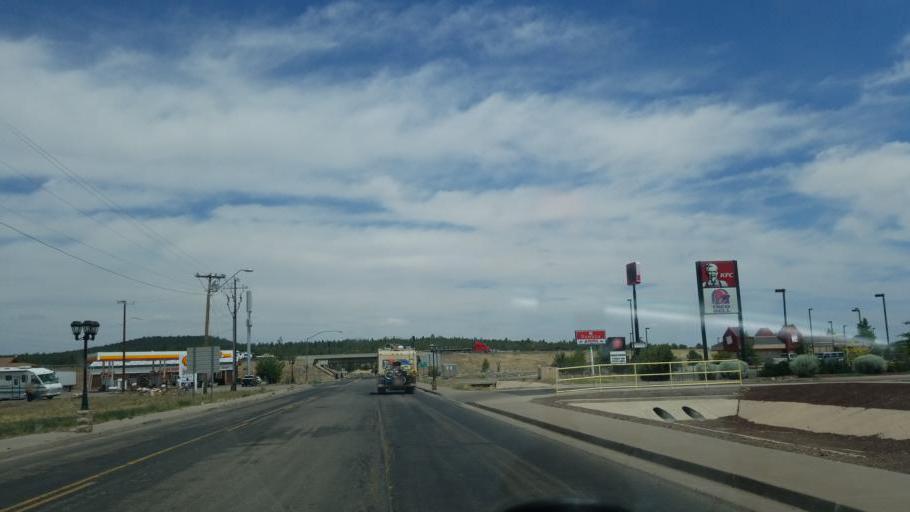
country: US
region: Arizona
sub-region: Coconino County
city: Williams
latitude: 35.2571
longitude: -112.1918
